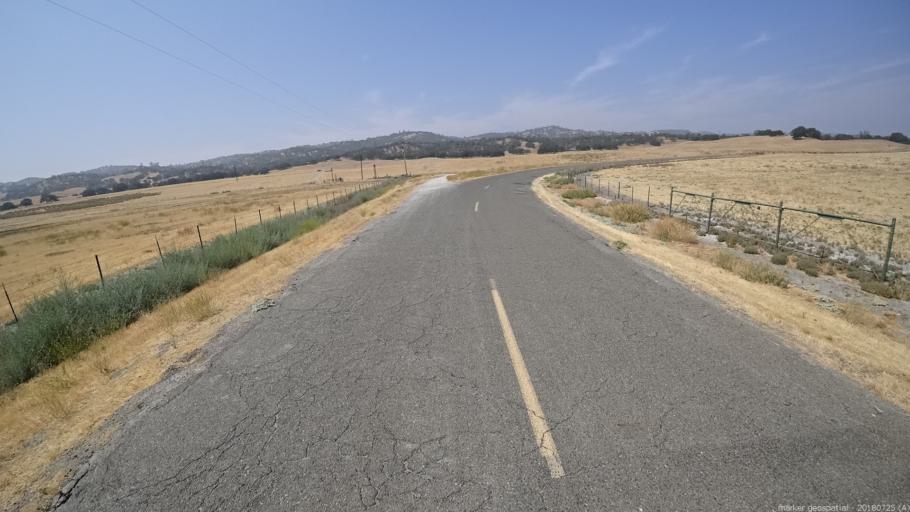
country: US
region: California
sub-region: San Luis Obispo County
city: Shandon
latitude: 35.8024
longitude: -120.3628
